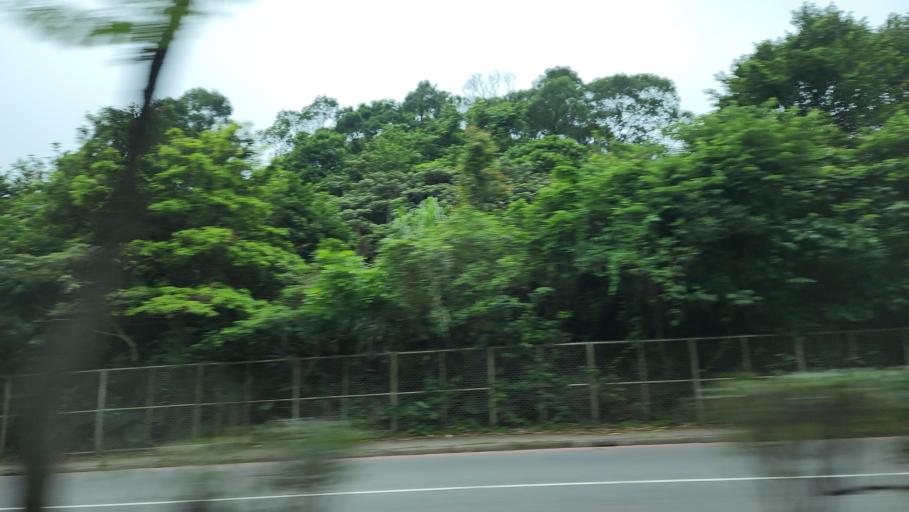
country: TW
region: Taiwan
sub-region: Keelung
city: Keelung
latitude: 25.1619
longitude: 121.6892
